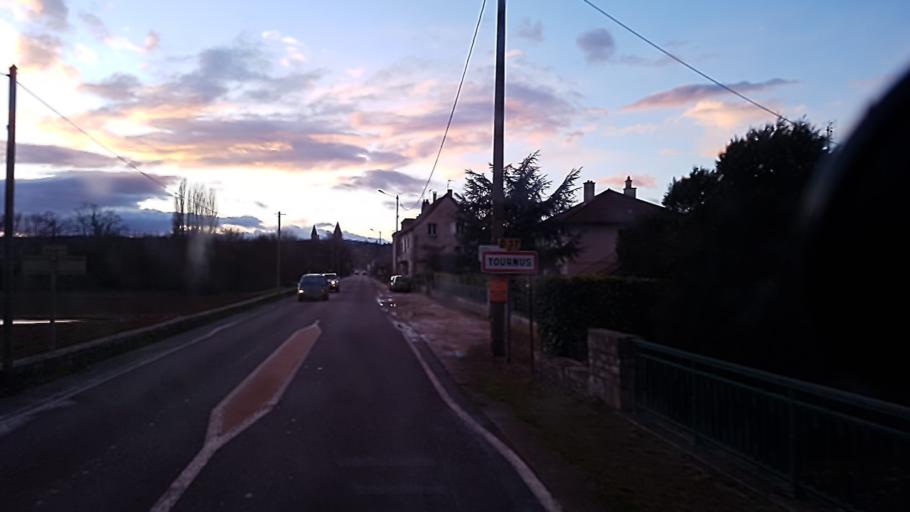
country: FR
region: Bourgogne
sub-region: Departement de Saone-et-Loire
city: Tournus
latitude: 46.5630
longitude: 4.9201
